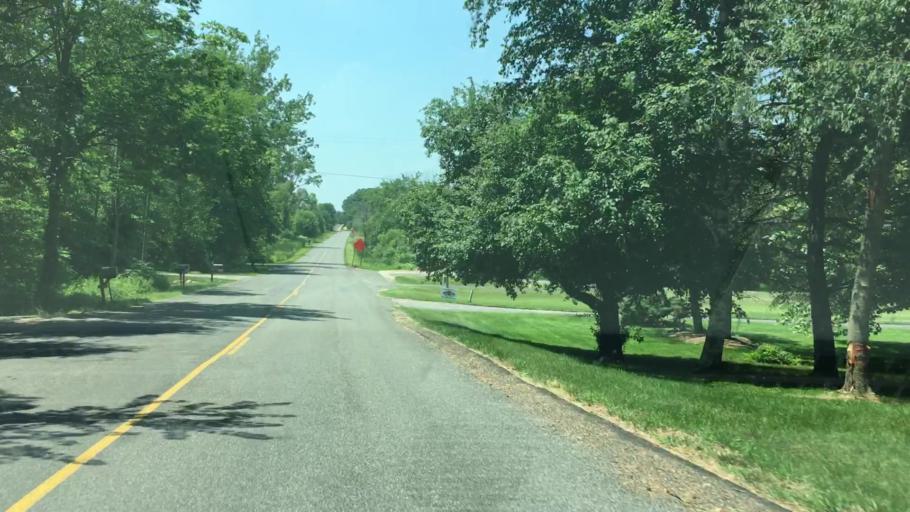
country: US
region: Michigan
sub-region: Kent County
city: Byron Center
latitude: 42.8411
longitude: -85.7756
